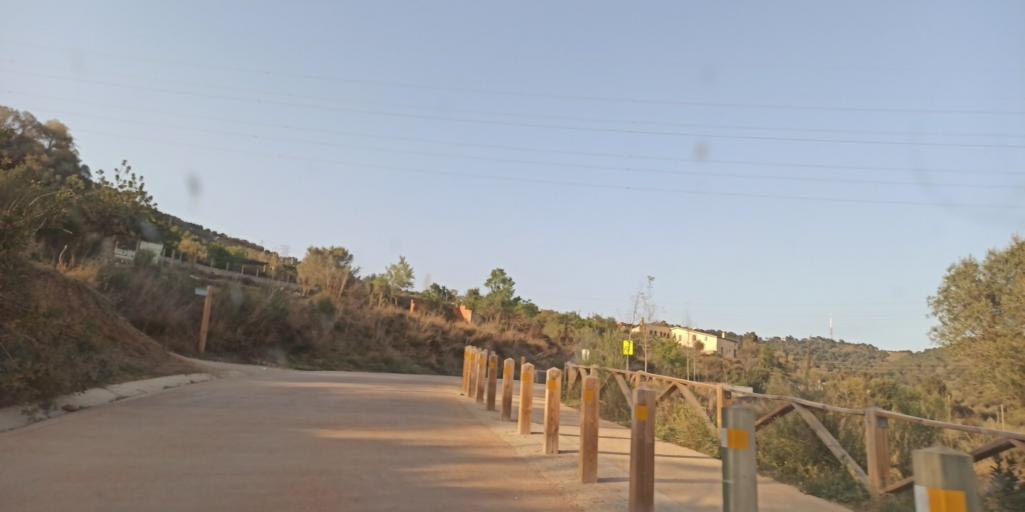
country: ES
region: Catalonia
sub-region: Provincia de Barcelona
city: Sant Just Desvern
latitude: 41.3964
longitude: 2.0826
